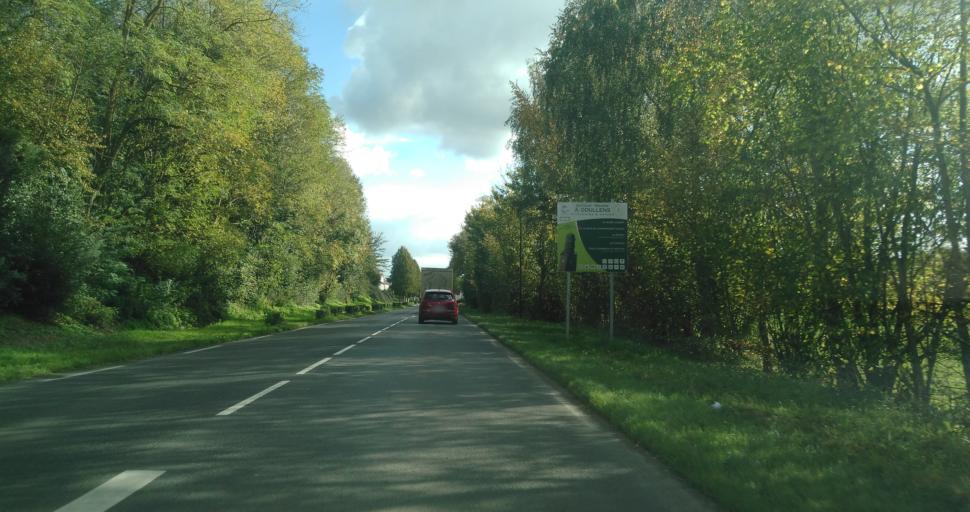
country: FR
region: Picardie
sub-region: Departement de la Somme
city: Doullens
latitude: 50.1632
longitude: 2.3266
